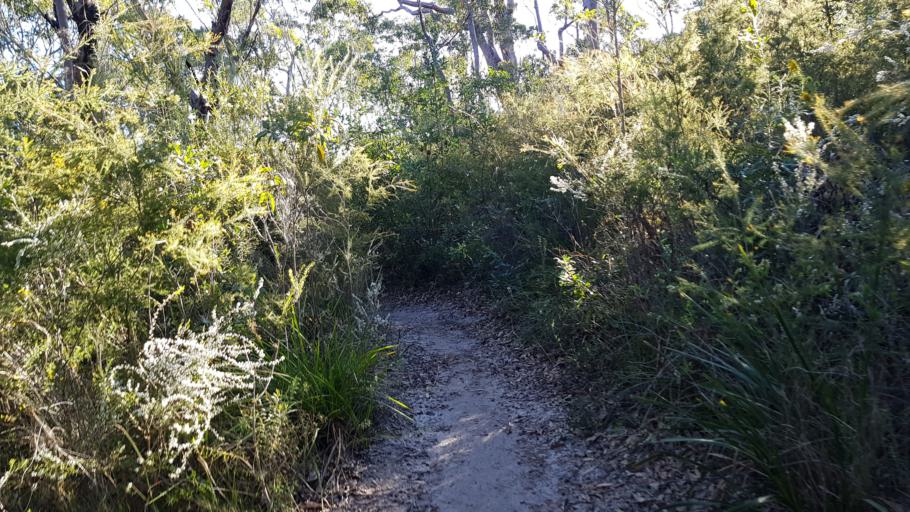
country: AU
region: New South Wales
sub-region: Willoughby
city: Chatswood West
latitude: -33.7984
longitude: 151.1516
